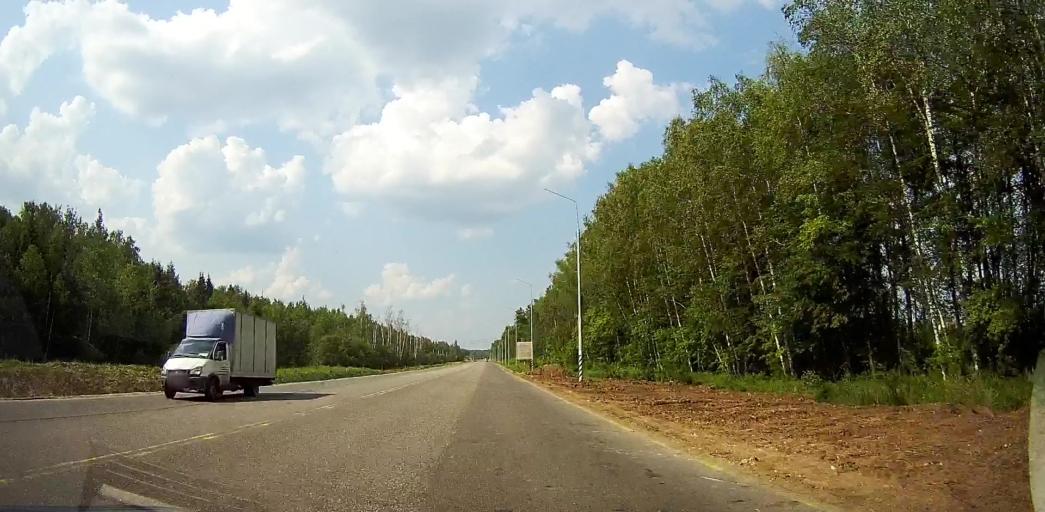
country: RU
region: Moskovskaya
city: Mikhnevo
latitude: 55.0635
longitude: 37.9539
